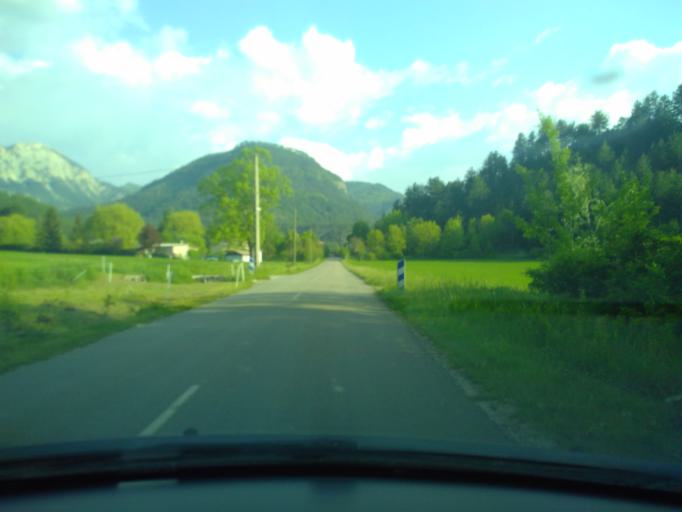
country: FR
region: Rhone-Alpes
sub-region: Departement de la Drome
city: Die
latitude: 44.6754
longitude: 5.4736
